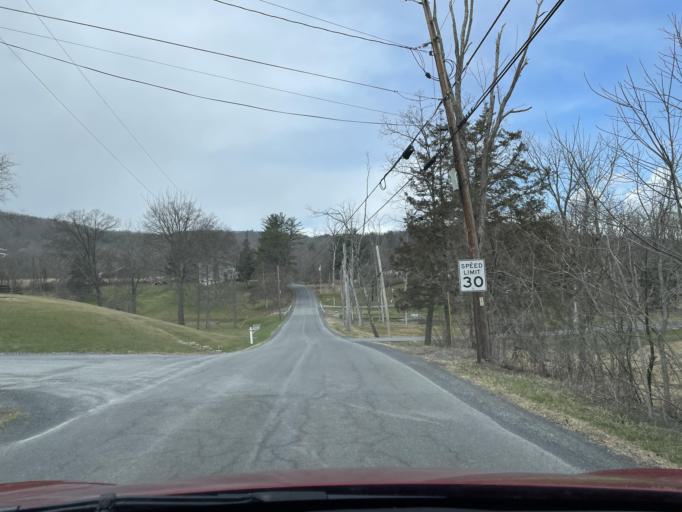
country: US
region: New York
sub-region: Ulster County
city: Saugerties
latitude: 42.1015
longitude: -73.9738
